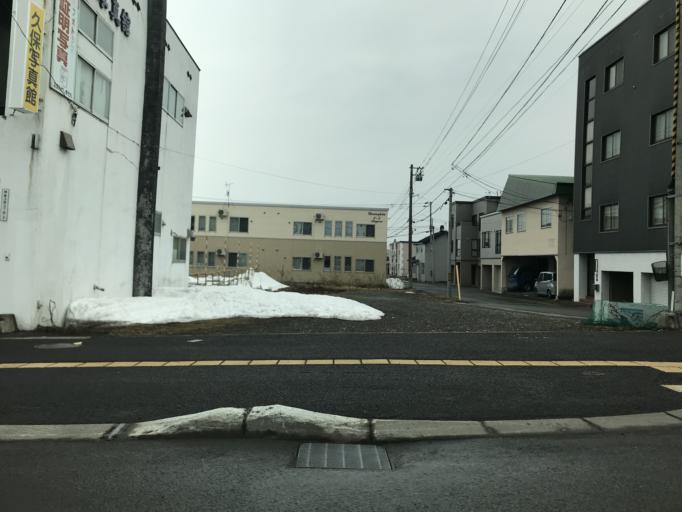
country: JP
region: Hokkaido
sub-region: Asahikawa-shi
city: Asahikawa
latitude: 43.7636
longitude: 142.3474
